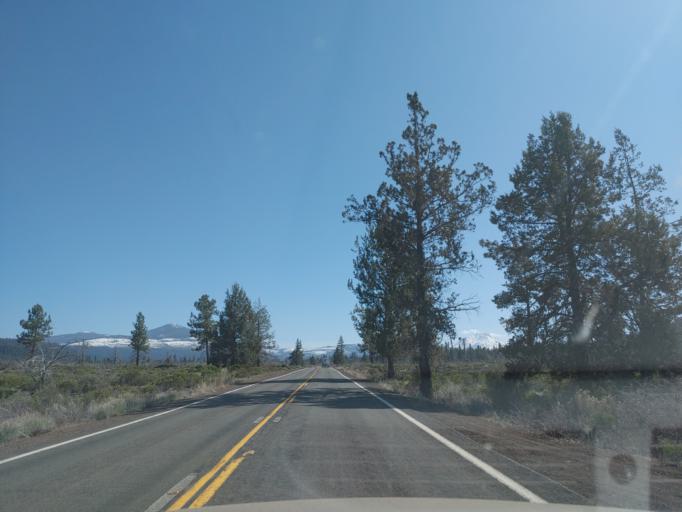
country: US
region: California
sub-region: Shasta County
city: Burney
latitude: 40.7011
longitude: -121.4181
